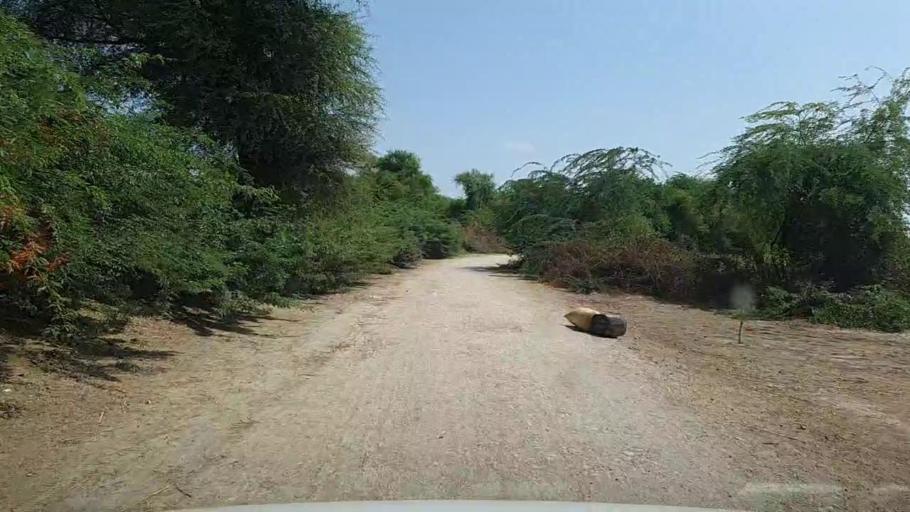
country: PK
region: Sindh
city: Kario
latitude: 24.8471
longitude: 68.6961
